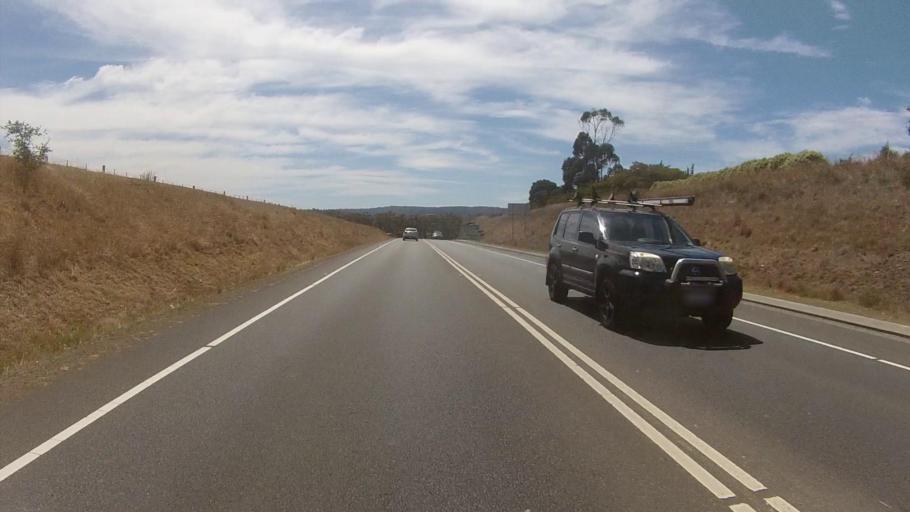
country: AU
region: Tasmania
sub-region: Kingborough
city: Kingston
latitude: -42.9899
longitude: 147.2857
